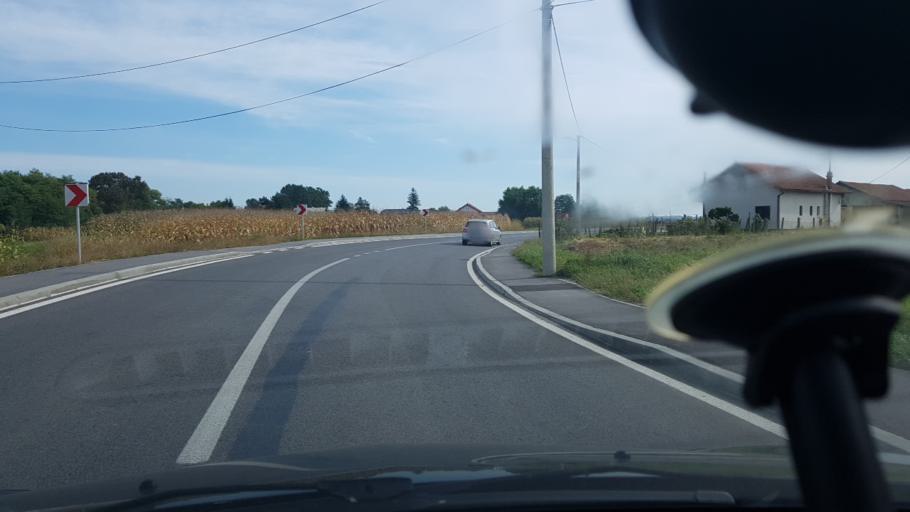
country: HR
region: Krapinsko-Zagorska
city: Marija Bistrica
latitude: 46.0546
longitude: 16.1423
